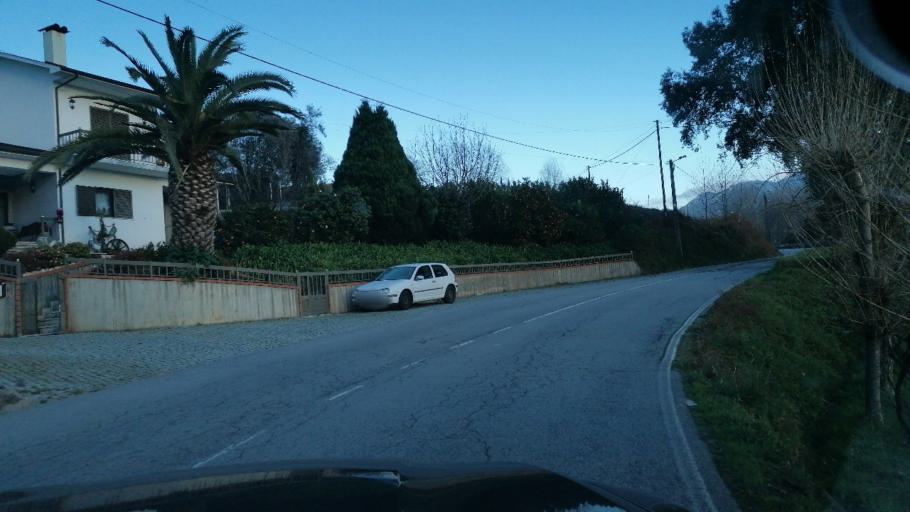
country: PT
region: Vila Real
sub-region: Mondim de Basto
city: Mondim de Basto
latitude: 41.4432
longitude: -7.9696
